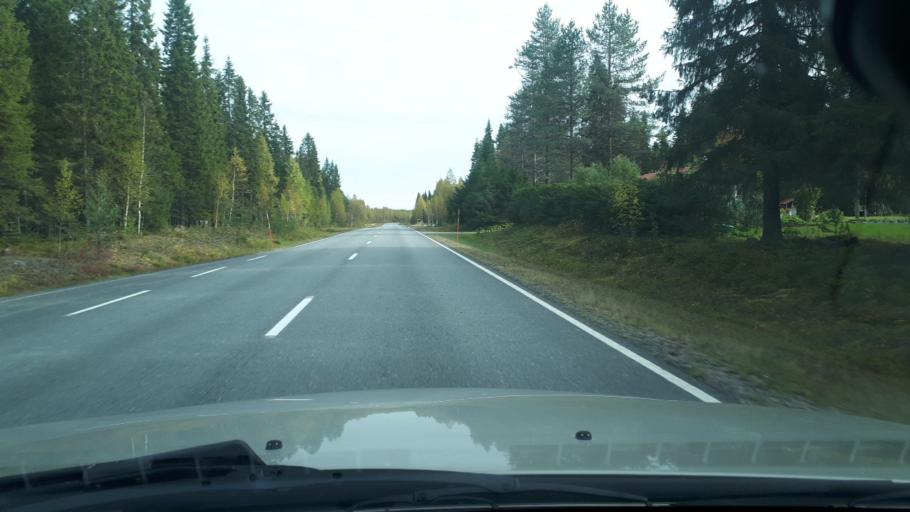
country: FI
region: Lapland
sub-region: Rovaniemi
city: Ranua
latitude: 65.9754
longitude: 26.1156
